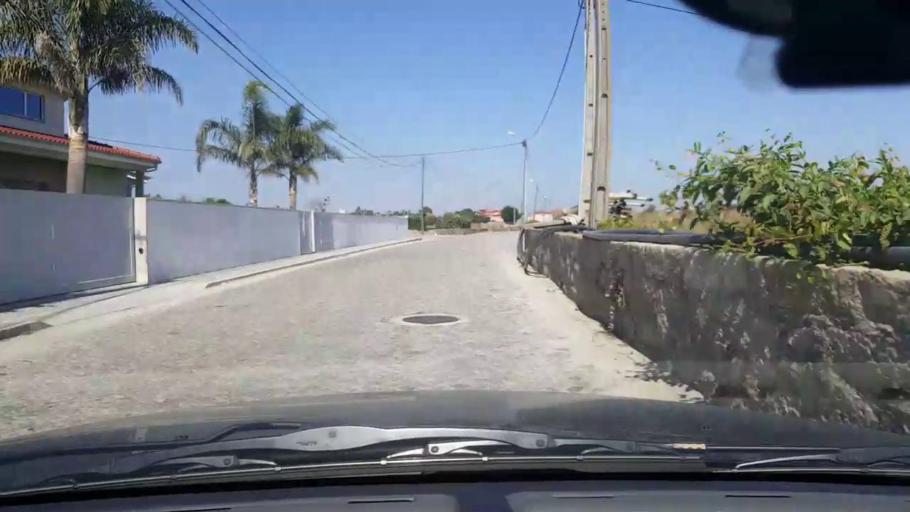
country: PT
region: Porto
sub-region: Matosinhos
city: Lavra
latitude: 41.2642
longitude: -8.6964
